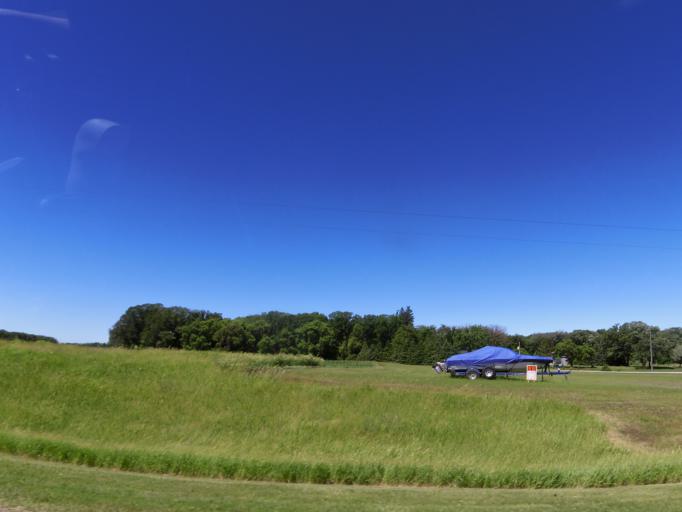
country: US
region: Minnesota
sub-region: Polk County
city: Fosston
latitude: 47.6196
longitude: -95.9828
